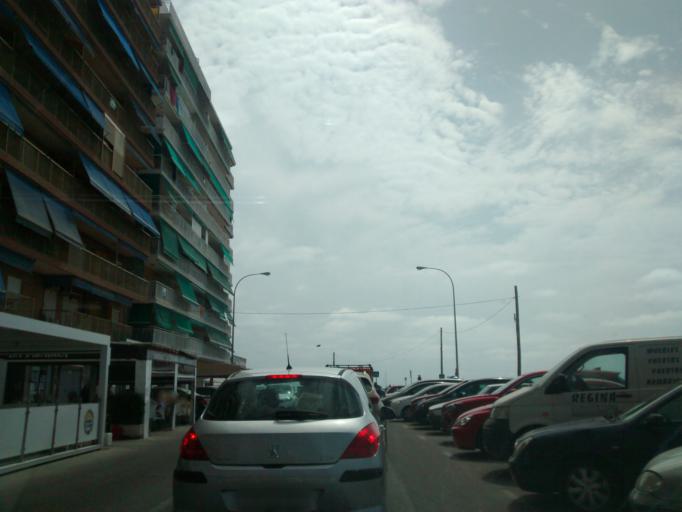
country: ES
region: Valencia
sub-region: Provincia de Alicante
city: Santa Pola
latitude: 38.1920
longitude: -0.5656
